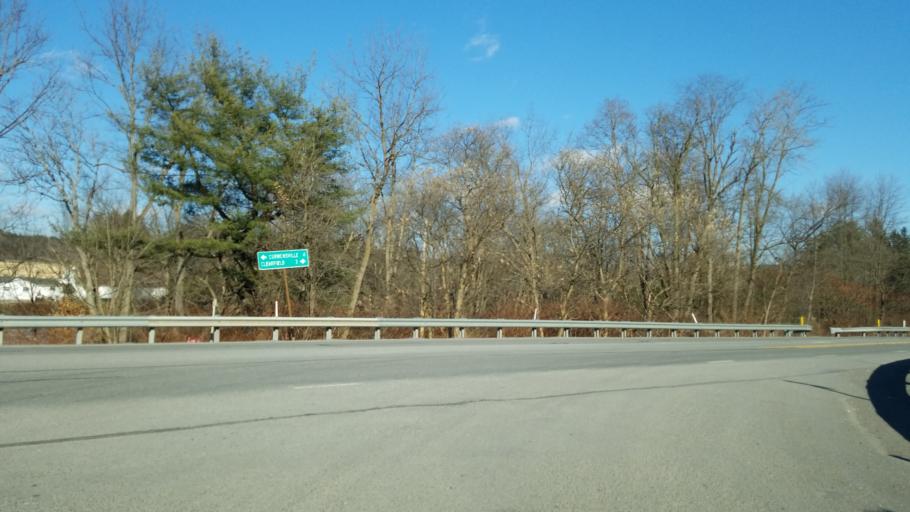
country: US
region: Pennsylvania
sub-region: Clearfield County
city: Hyde
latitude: 40.9956
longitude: -78.4632
